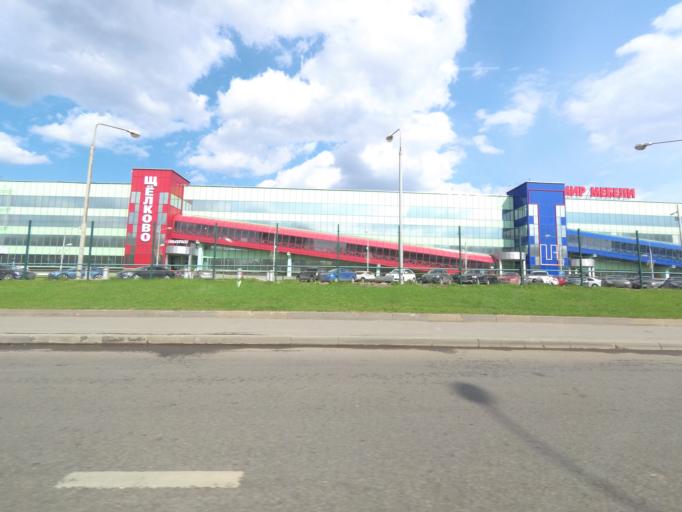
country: RU
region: Moscow
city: Gol'yanovo
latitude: 55.8059
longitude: 37.8301
